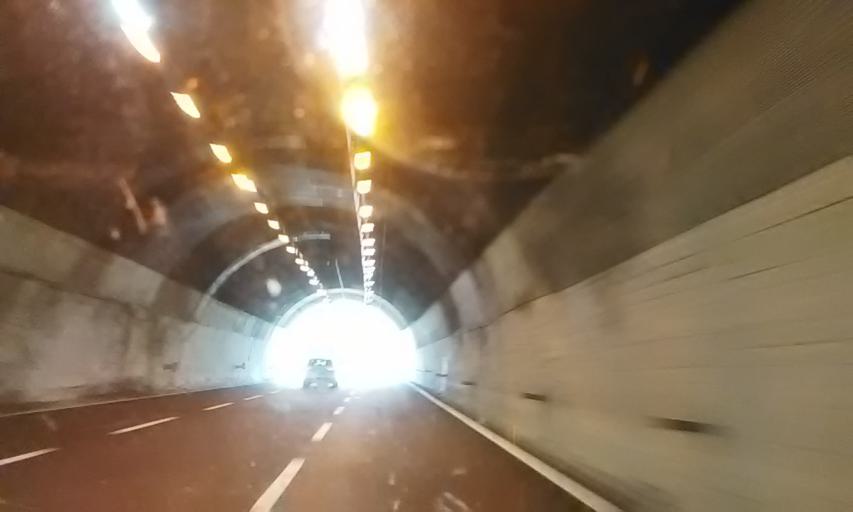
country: IT
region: Liguria
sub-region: Provincia di Savona
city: Albisola Superiore
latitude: 44.3354
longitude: 8.5259
